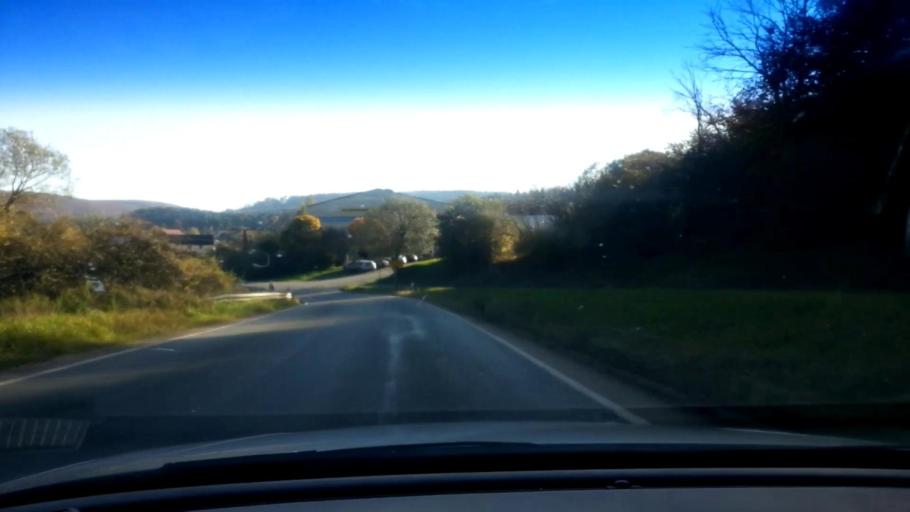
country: DE
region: Bavaria
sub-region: Upper Franconia
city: Poxdorf
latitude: 49.8877
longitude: 11.1280
